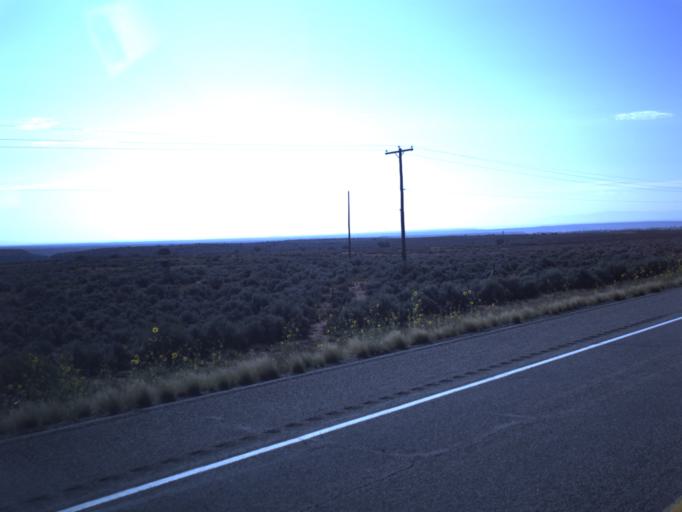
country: US
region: Utah
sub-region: San Juan County
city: Blanding
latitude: 37.5183
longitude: -109.4941
